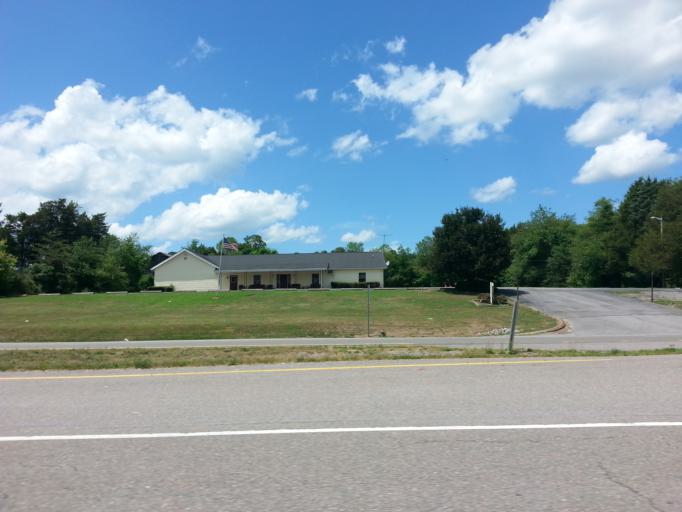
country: US
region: Virginia
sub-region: Lee County
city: Jonesville
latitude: 36.6720
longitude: -83.1801
